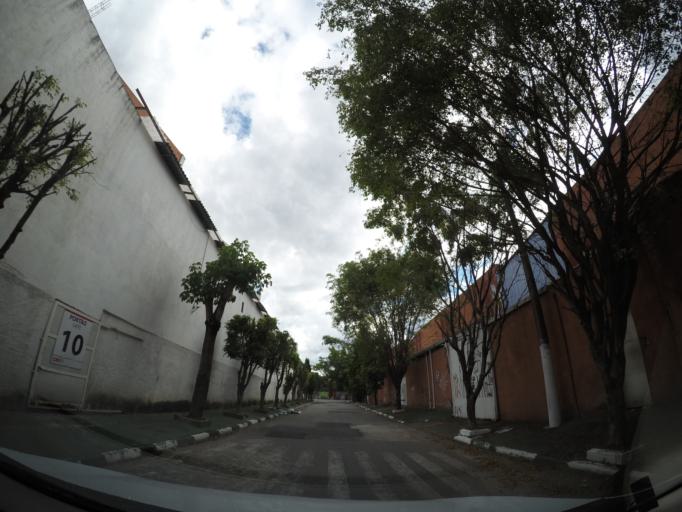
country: BR
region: Sao Paulo
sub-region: Guarulhos
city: Guarulhos
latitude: -23.4812
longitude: -46.5544
